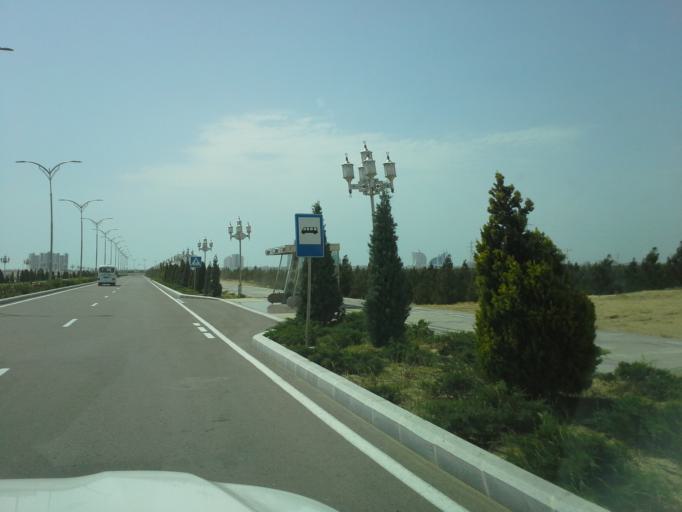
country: TM
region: Balkan
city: Turkmenbasy
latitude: 39.9661
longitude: 52.8558
